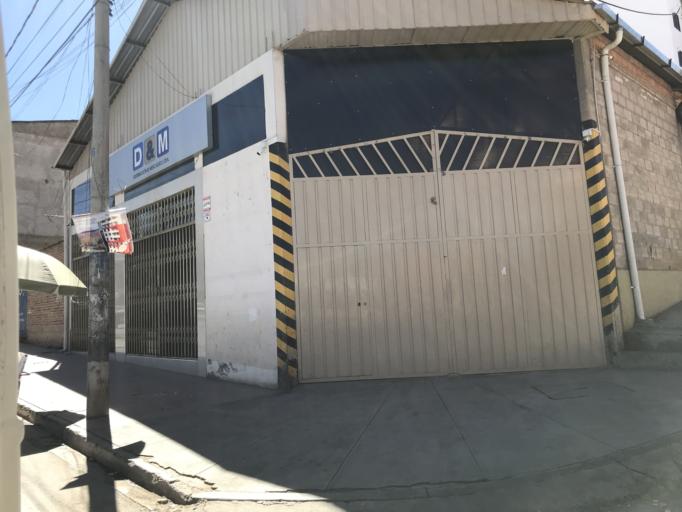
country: BO
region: Chuquisaca
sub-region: Provincia Oropeza
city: Huata
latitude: -19.0236
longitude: -65.2472
